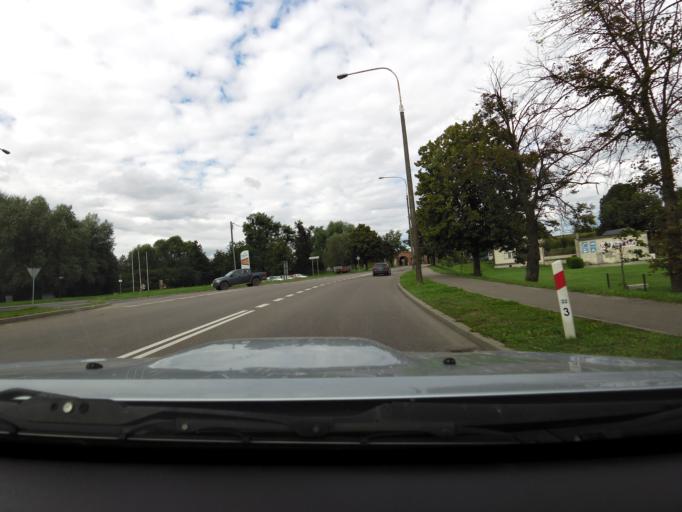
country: PL
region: Pomeranian Voivodeship
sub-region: Powiat malborski
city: Malbork
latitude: 54.0453
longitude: 19.0239
